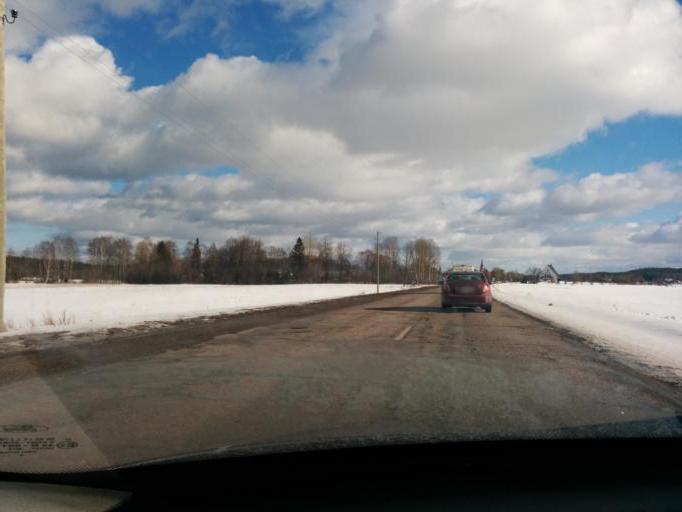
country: LV
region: Cesvaine
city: Cesvaine
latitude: 57.2402
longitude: 26.3847
